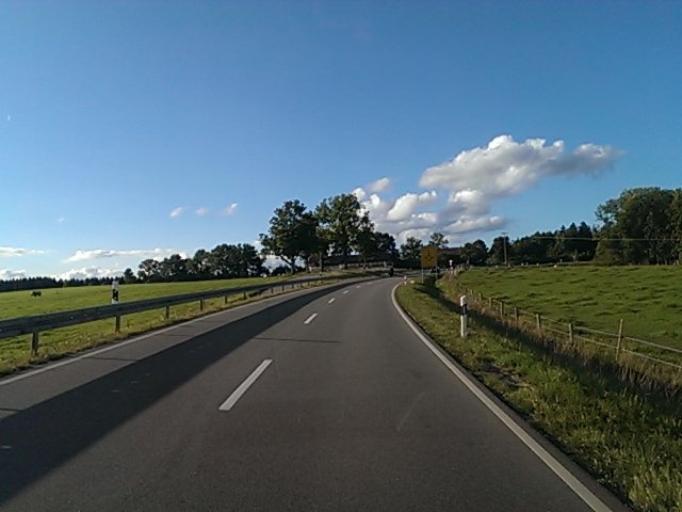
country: DE
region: Baden-Wuerttemberg
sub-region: Karlsruhe Region
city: Lossburg
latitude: 48.3707
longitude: 8.4463
